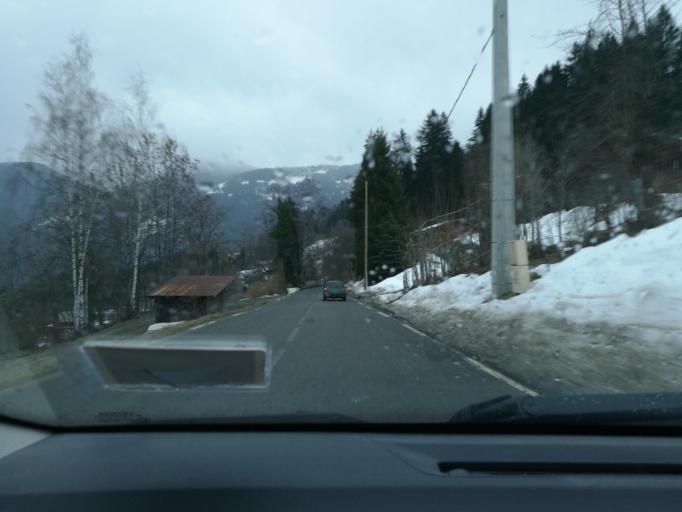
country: FR
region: Rhone-Alpes
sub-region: Departement de la Haute-Savoie
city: Passy
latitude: 45.8908
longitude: 6.6786
